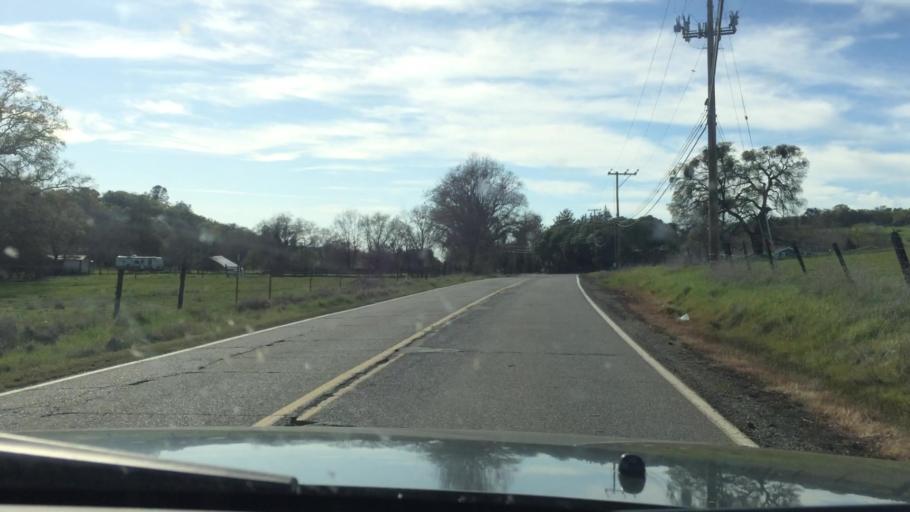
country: US
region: California
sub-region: Amador County
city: Plymouth
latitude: 38.4803
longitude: -120.8563
